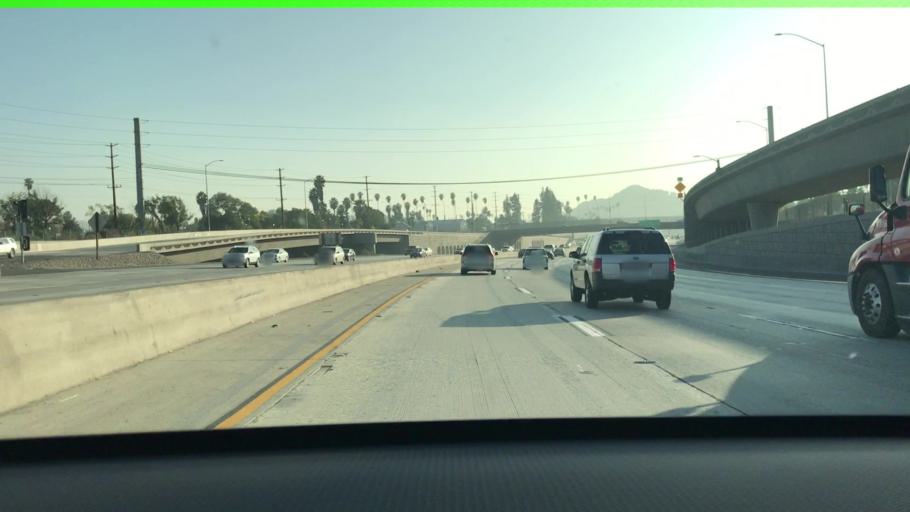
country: US
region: California
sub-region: Riverside County
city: Riverside
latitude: 33.9764
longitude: -117.3719
